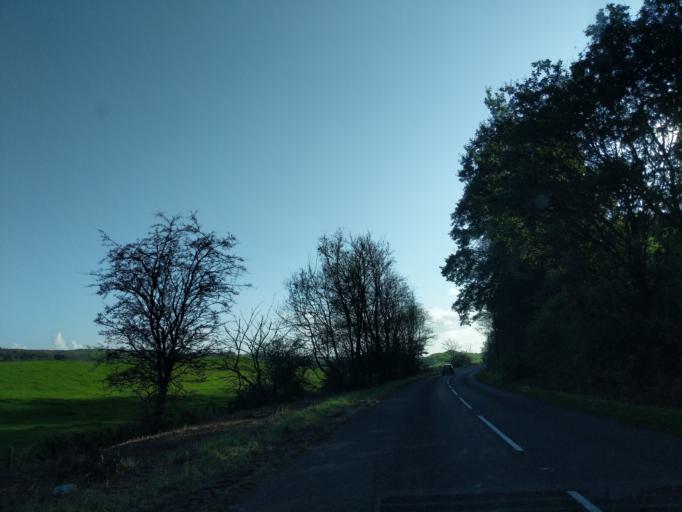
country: GB
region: Scotland
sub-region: Dumfries and Galloway
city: Kirkcudbright
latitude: 54.8876
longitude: -4.0174
